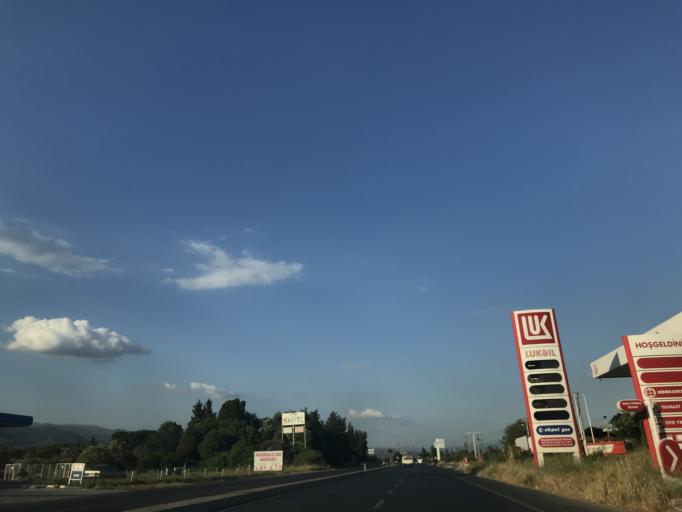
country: TR
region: Aydin
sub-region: Sultanhisar Ilcesi
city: Salavatli
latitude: 37.8607
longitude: 28.1069
